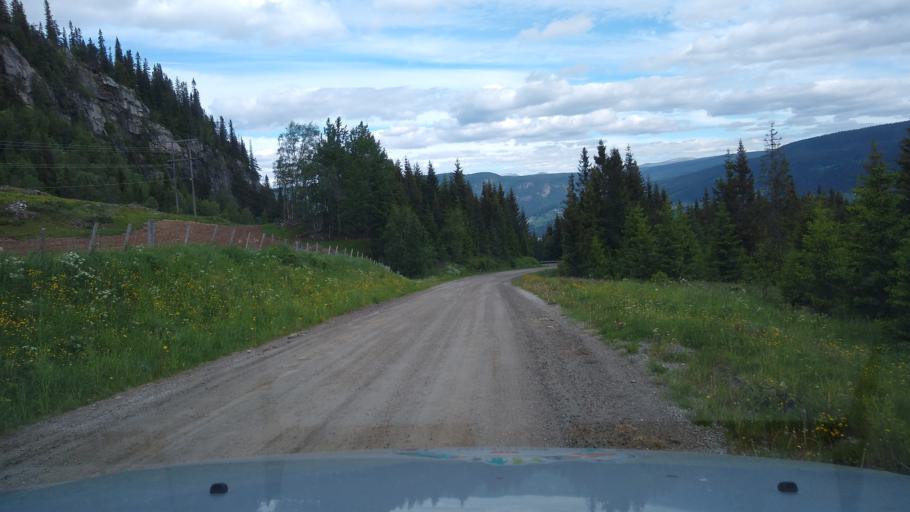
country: NO
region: Oppland
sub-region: Ringebu
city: Ringebu
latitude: 61.4946
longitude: 10.1453
